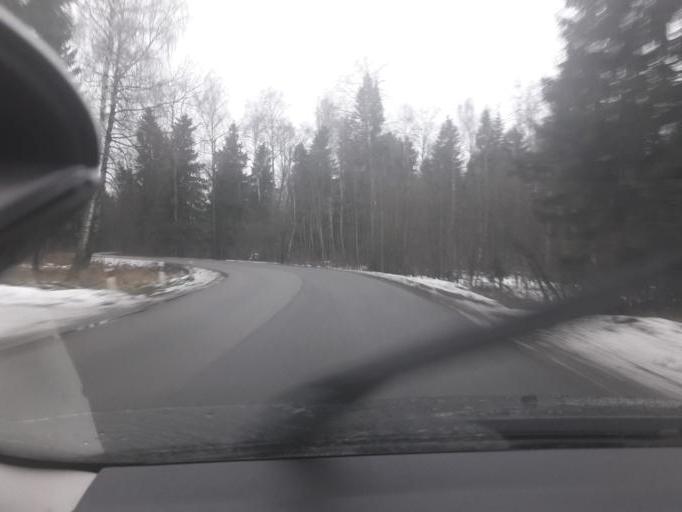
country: RU
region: Moskovskaya
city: Fryazevo
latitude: 55.7591
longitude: 38.5154
